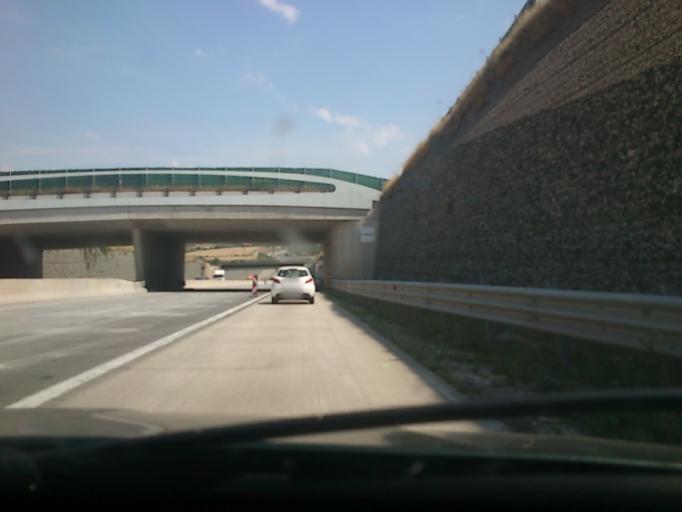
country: AT
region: Lower Austria
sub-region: Politischer Bezirk Mistelbach
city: Wolkersdorf im Weinviertel
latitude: 48.3886
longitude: 16.4982
